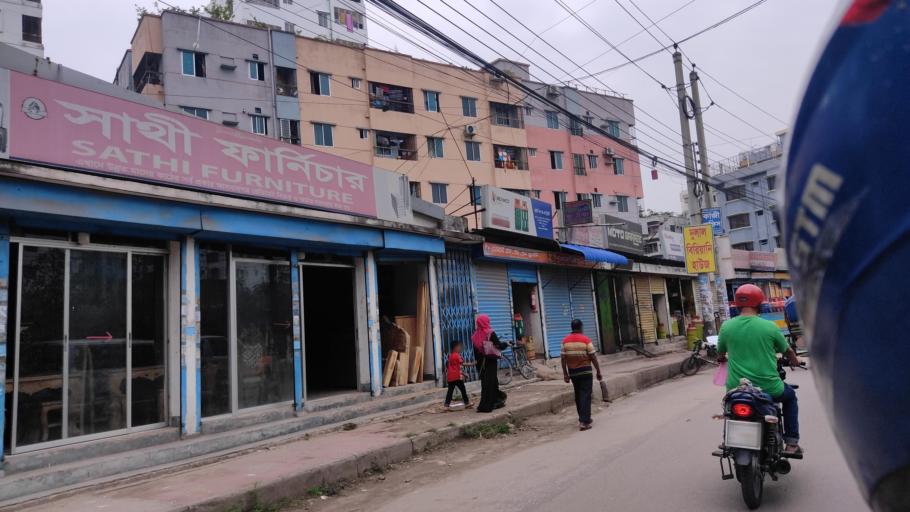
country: BD
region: Dhaka
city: Azimpur
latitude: 23.7835
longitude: 90.3682
